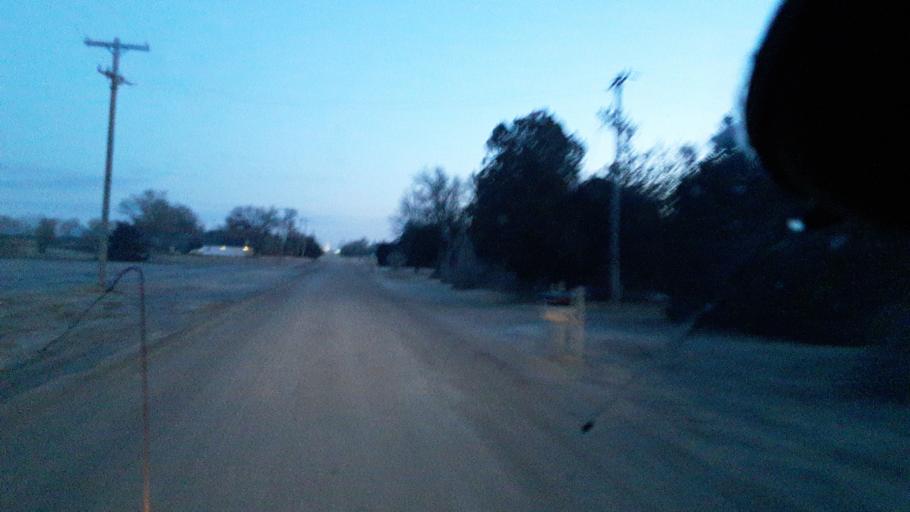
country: US
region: Kansas
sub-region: Reno County
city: South Hutchinson
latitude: 37.9998
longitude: -97.9772
